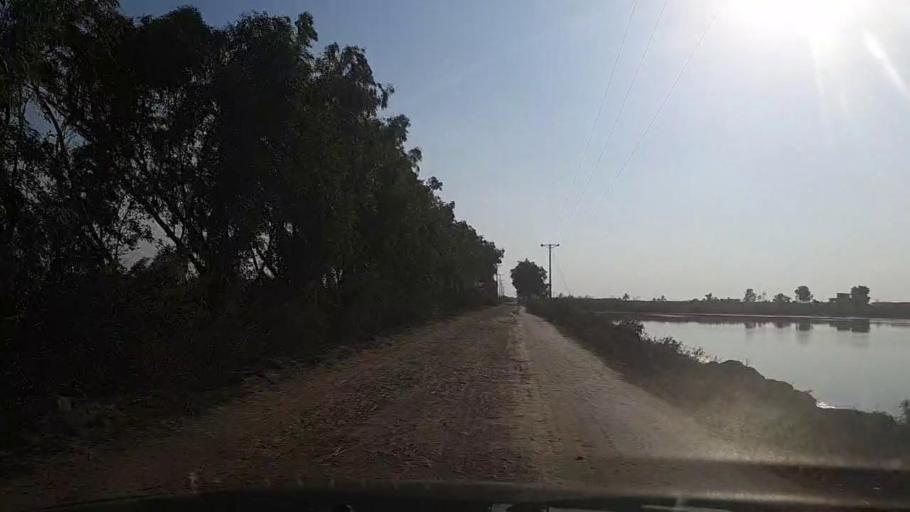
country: PK
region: Sindh
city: Gharo
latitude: 24.7195
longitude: 67.6897
